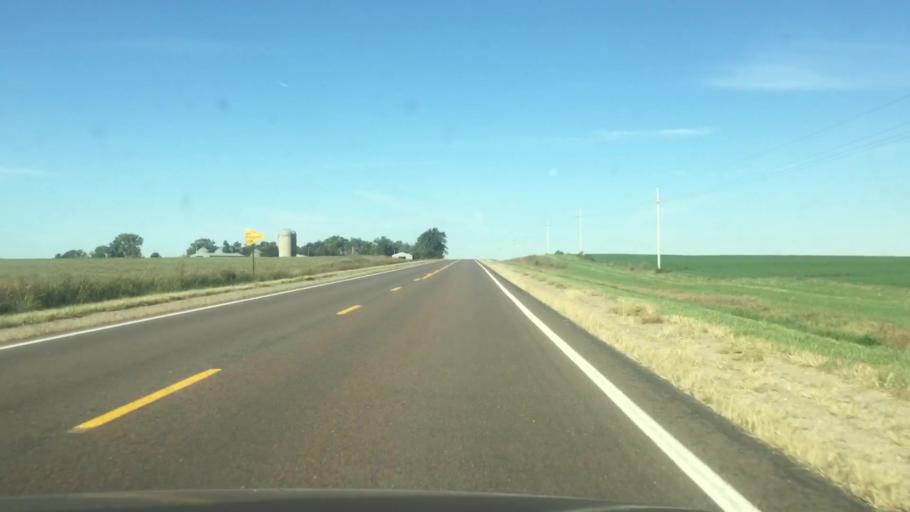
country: US
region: Nebraska
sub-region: Jefferson County
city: Fairbury
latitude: 40.1472
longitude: -97.3631
